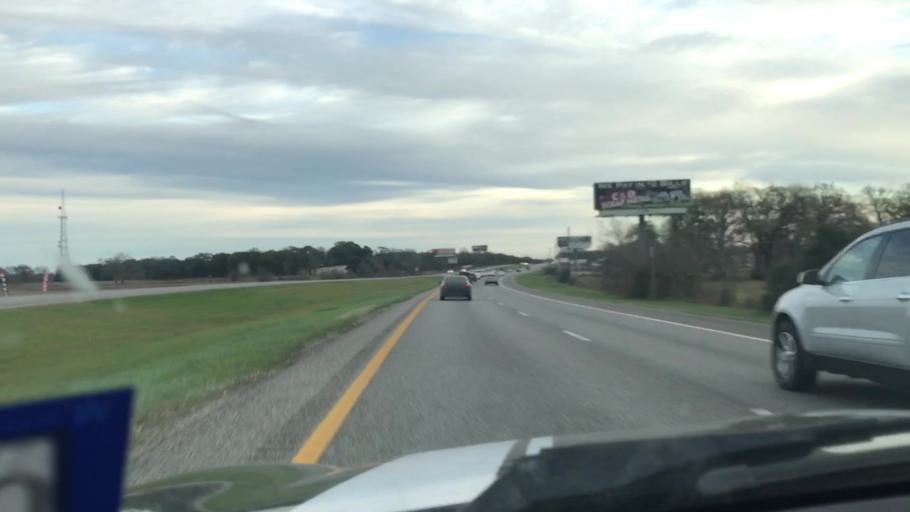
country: US
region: Texas
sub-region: Waller County
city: Hempstead
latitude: 30.1300
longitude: -96.1406
